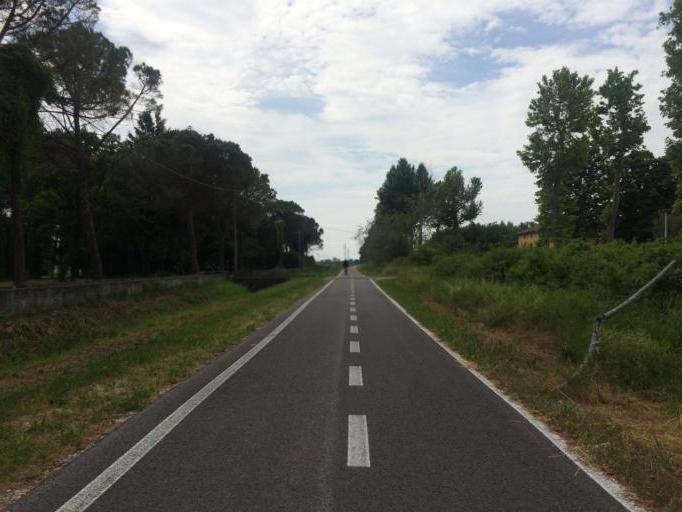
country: IT
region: Friuli Venezia Giulia
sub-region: Provincia di Udine
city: Aquileia
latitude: 45.7445
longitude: 13.3823
